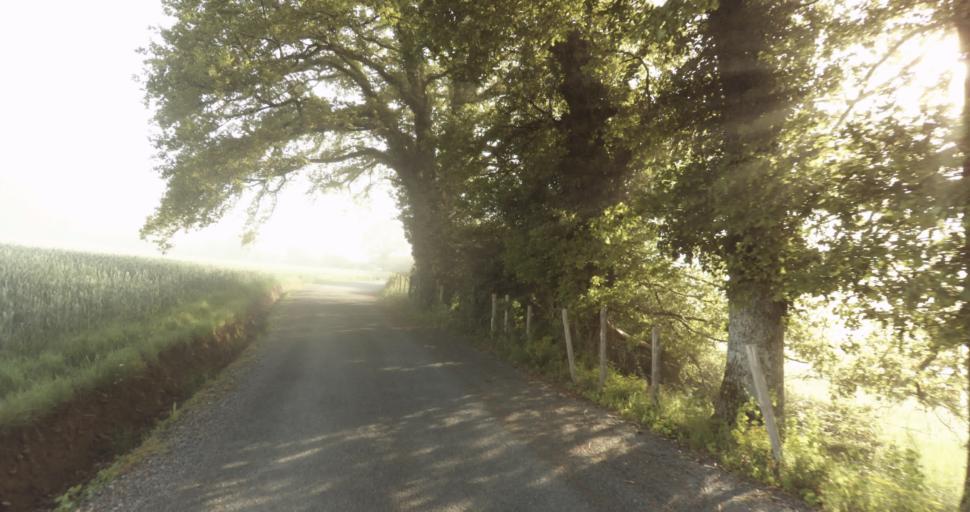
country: FR
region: Limousin
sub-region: Departement de la Haute-Vienne
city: Condat-sur-Vienne
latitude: 45.7731
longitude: 1.2852
